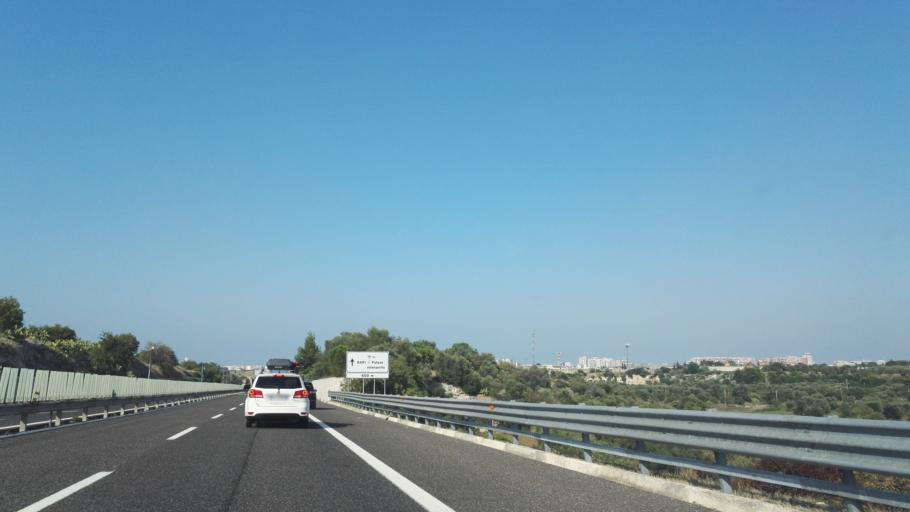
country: IT
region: Apulia
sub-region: Provincia di Bari
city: Modugno
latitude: 41.0944
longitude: 16.8192
